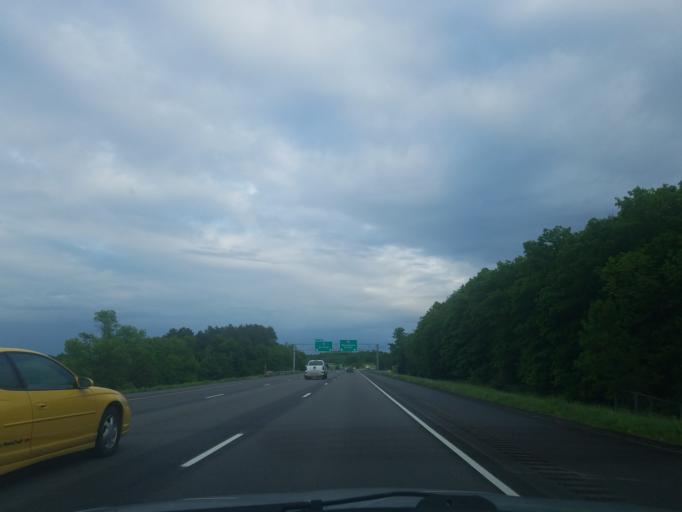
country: US
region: Minnesota
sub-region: Stearns County
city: Collegeville
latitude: 45.5876
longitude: -94.3670
